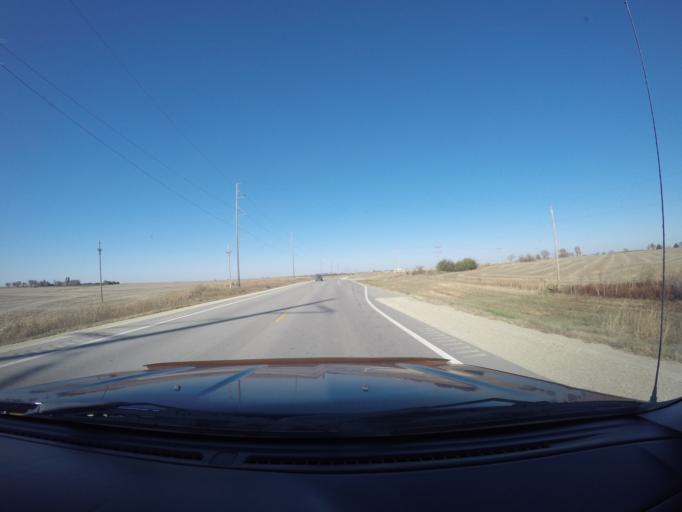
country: US
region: Kansas
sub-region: Riley County
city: Ogden
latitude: 39.2791
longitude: -96.7371
